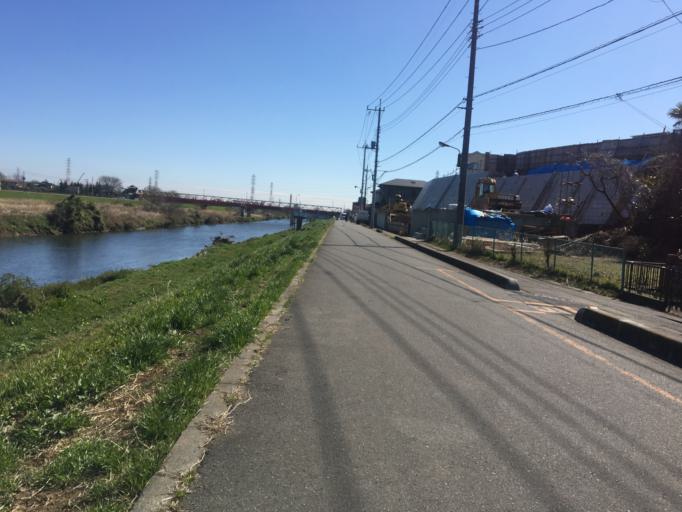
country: JP
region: Saitama
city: Shiki
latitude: 35.8310
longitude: 139.5868
